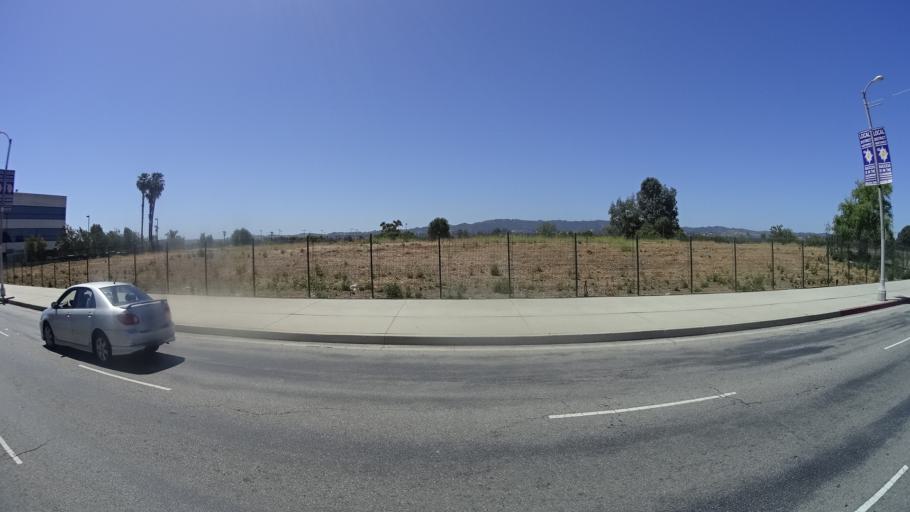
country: US
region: California
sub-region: Los Angeles County
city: Northridge
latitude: 34.1866
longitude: -118.5049
